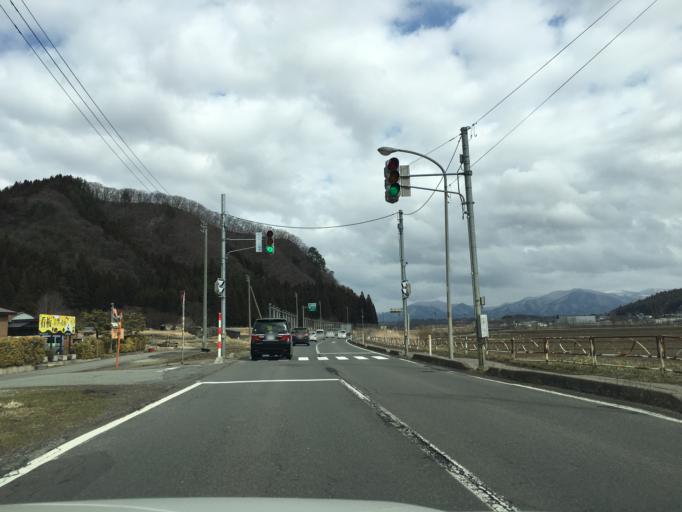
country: JP
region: Akita
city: Hanawa
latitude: 40.2462
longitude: 140.7434
